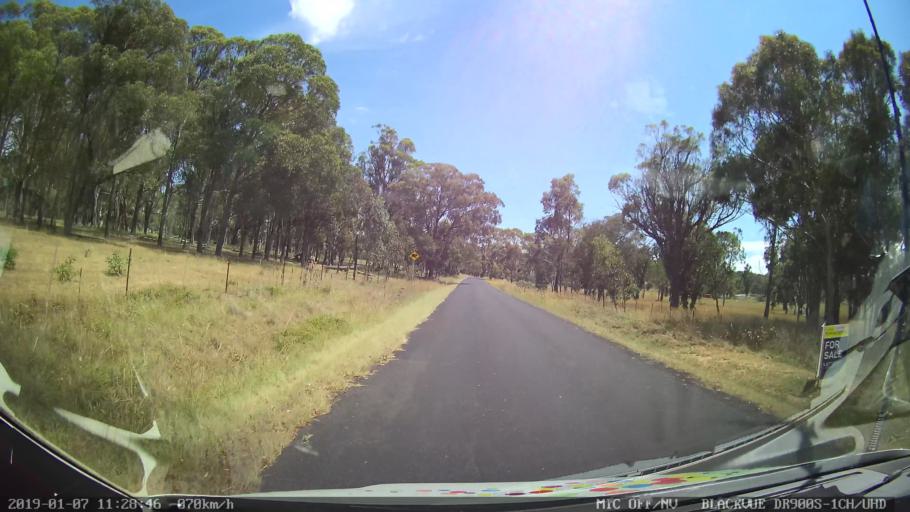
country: AU
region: New South Wales
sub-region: Armidale Dumaresq
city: Armidale
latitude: -30.4453
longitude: 151.5652
